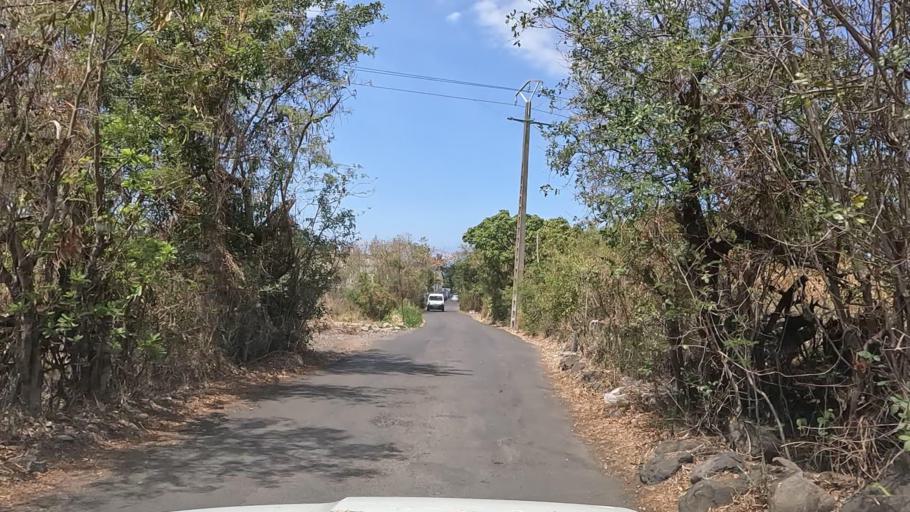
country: RE
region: Reunion
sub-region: Reunion
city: Saint-Louis
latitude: -21.2792
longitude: 55.4446
